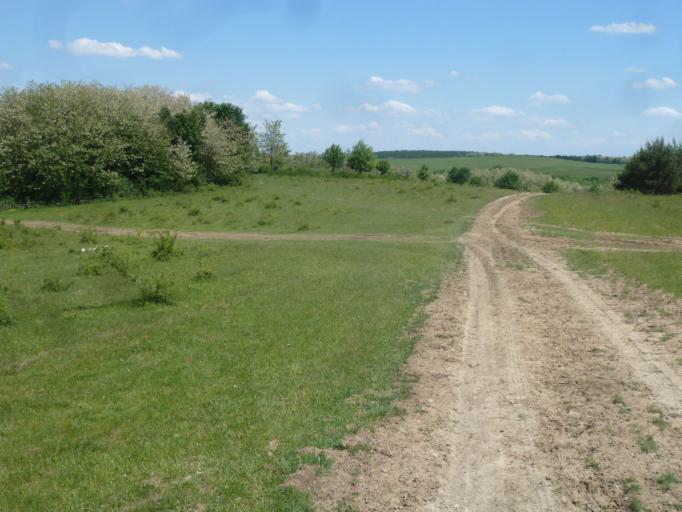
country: SK
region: Kosicky
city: Moldava nad Bodvou
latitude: 48.5104
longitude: 21.0568
